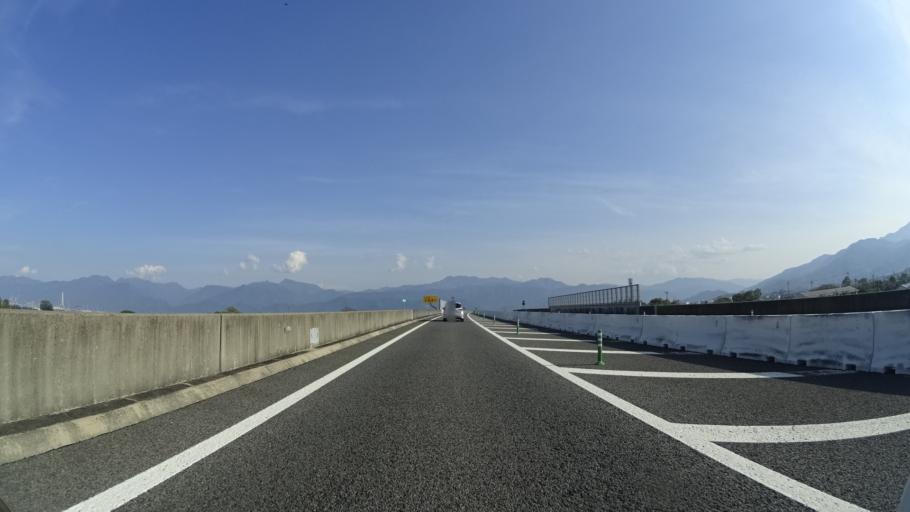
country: JP
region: Ehime
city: Saijo
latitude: 33.9523
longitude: 133.0688
